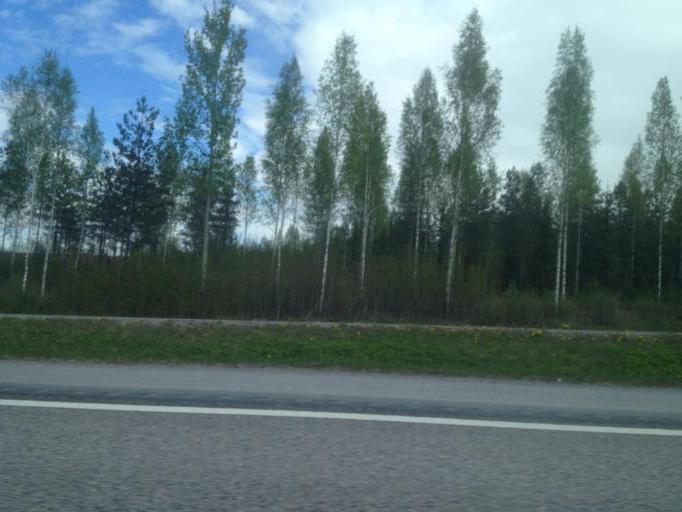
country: FI
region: Haeme
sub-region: Riihimaeki
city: Riihimaeki
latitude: 60.6623
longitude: 24.7917
